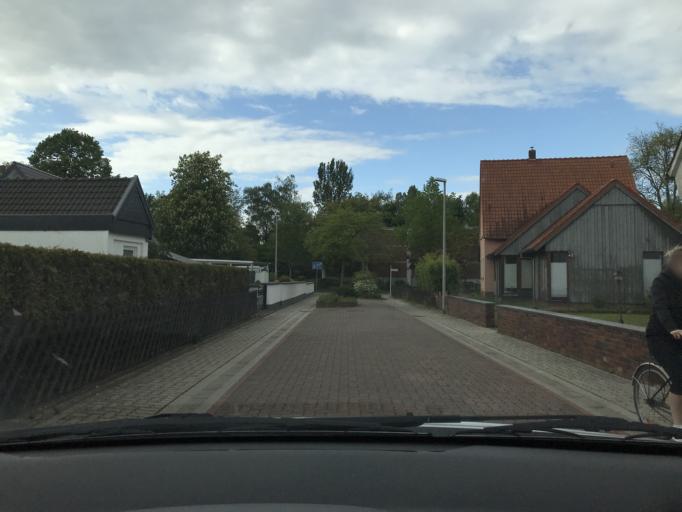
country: DE
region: North Rhine-Westphalia
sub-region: Regierungsbezirk Detmold
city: Minden
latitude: 52.2812
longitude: 8.8967
